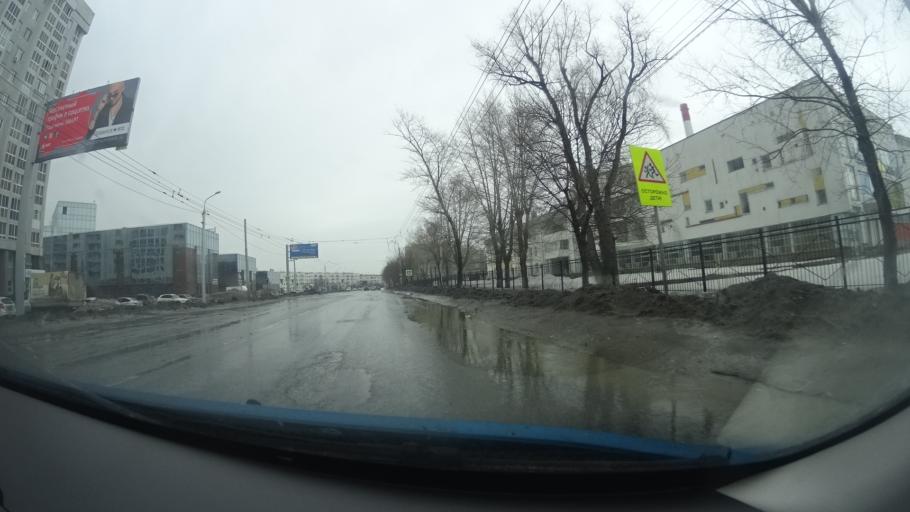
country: RU
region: Bashkortostan
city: Ufa
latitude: 54.7128
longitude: 56.0016
